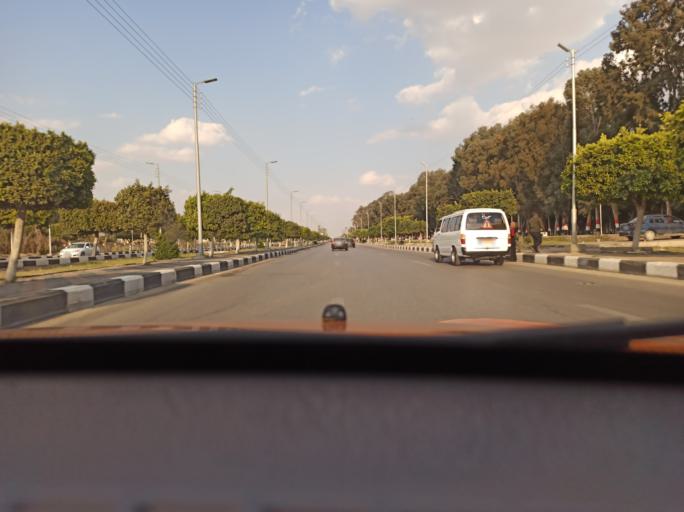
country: EG
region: Al Isma'iliyah
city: Ismailia
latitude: 30.6174
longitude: 32.2652
